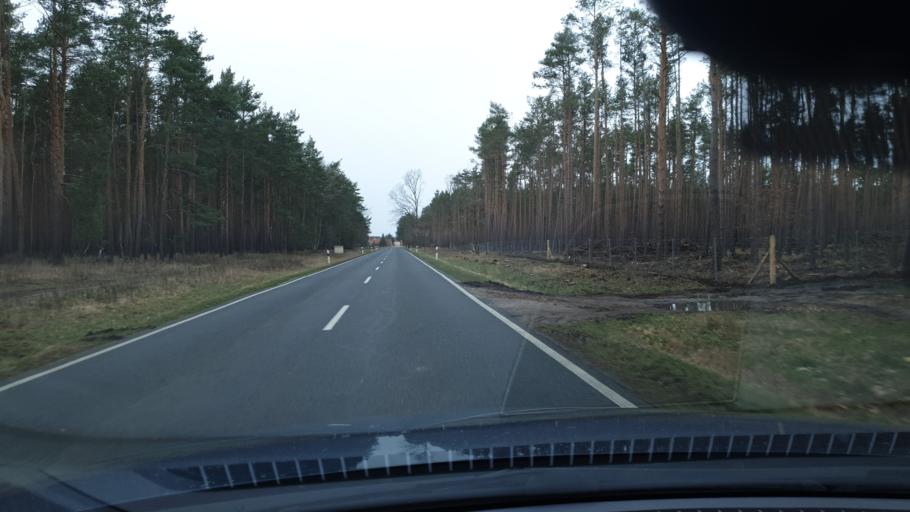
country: DE
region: Saxony-Anhalt
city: Radis
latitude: 51.7756
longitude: 12.4911
